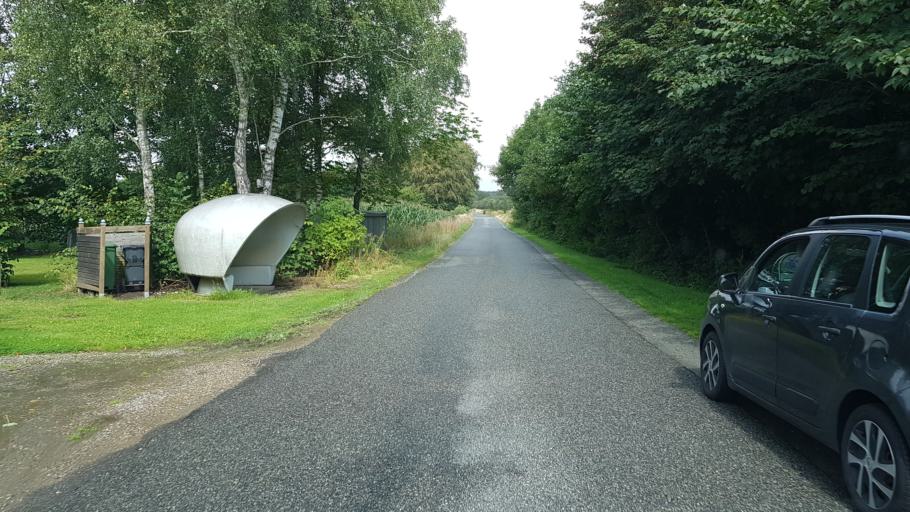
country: DK
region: South Denmark
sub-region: Vejen Kommune
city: Holsted
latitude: 55.5004
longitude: 8.9565
